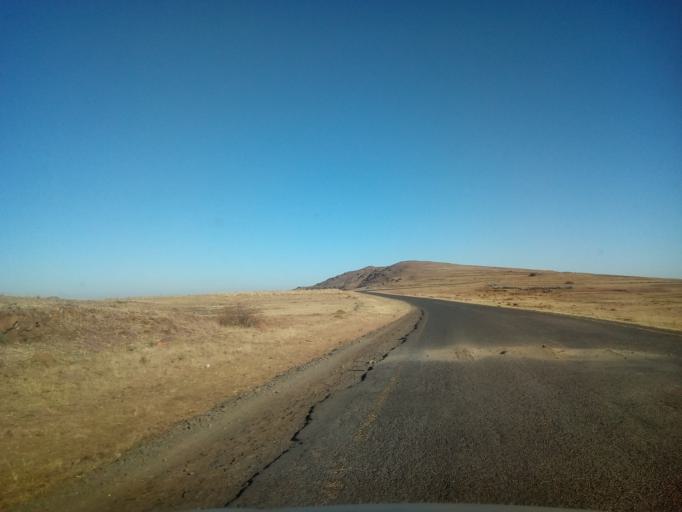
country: LS
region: Berea
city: Teyateyaneng
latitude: -29.2542
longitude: 27.7785
